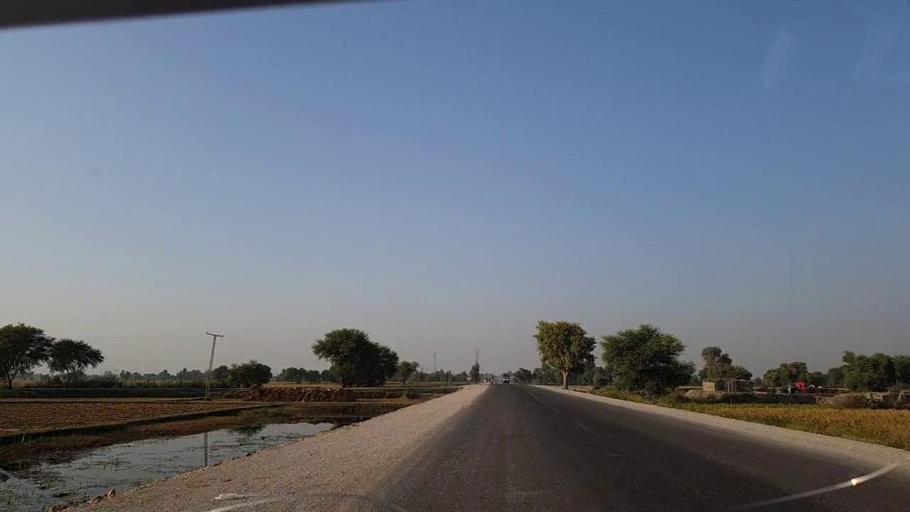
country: PK
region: Sindh
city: Rustam jo Goth
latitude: 27.9546
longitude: 68.8082
